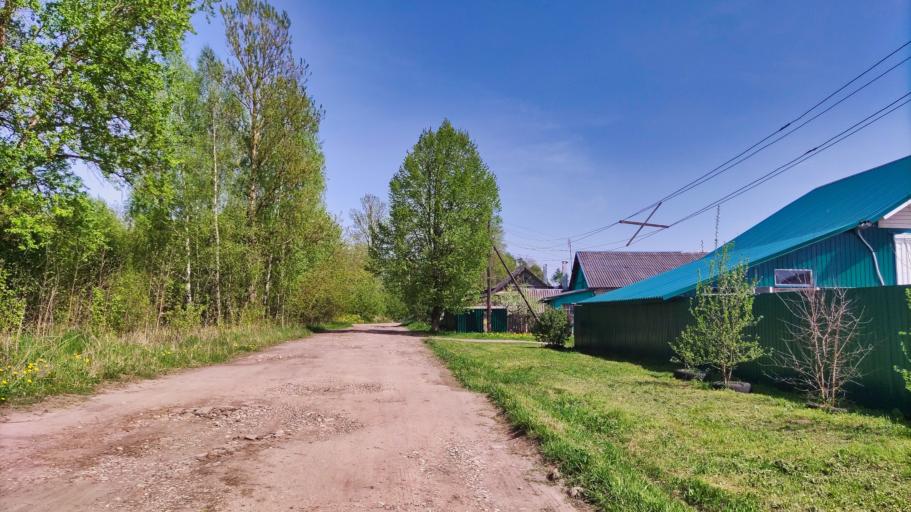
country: RU
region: Tverskaya
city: Rzhev
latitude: 56.2365
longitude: 34.3109
